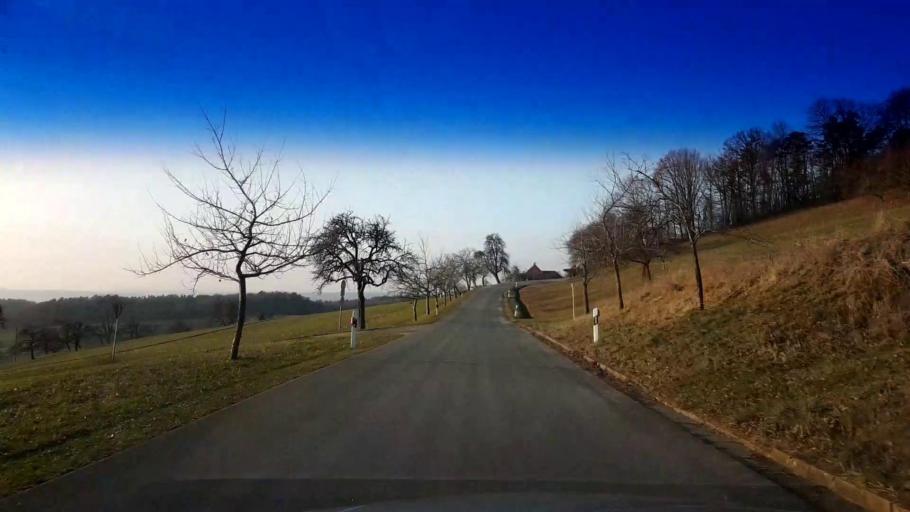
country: DE
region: Bavaria
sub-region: Upper Franconia
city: Schesslitz
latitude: 50.0139
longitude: 11.0278
